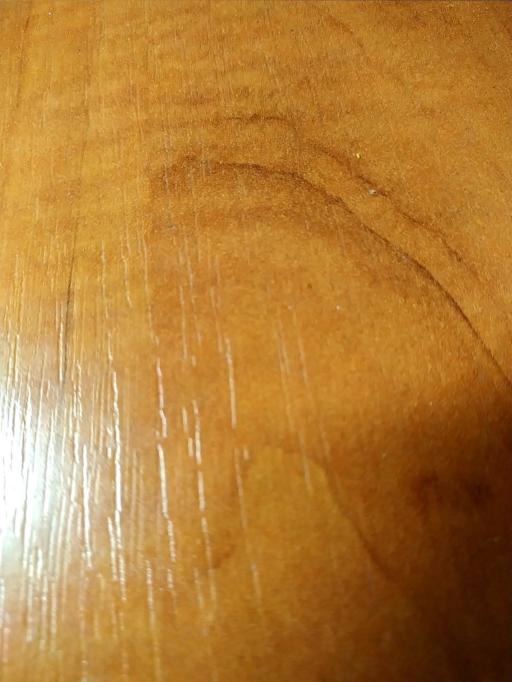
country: RU
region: Smolensk
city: Yartsevo
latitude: 55.4346
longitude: 32.7989
